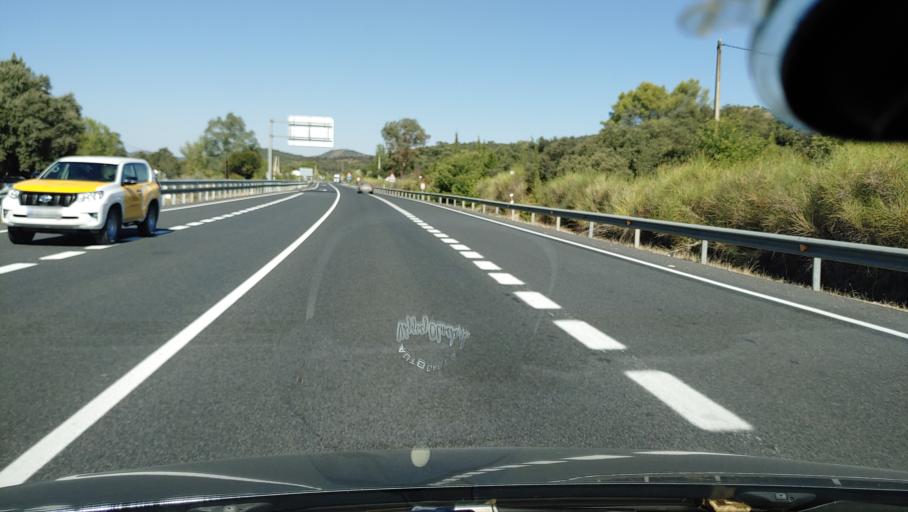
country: ES
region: Andalusia
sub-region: Province of Cordoba
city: Villaharta
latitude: 38.1276
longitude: -4.9049
